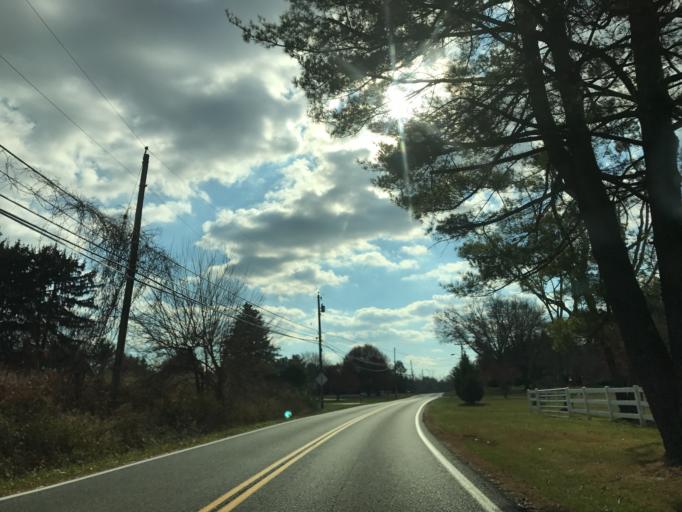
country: US
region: Maryland
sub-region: Harford County
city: Pleasant Hills
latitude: 39.4973
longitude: -76.3722
